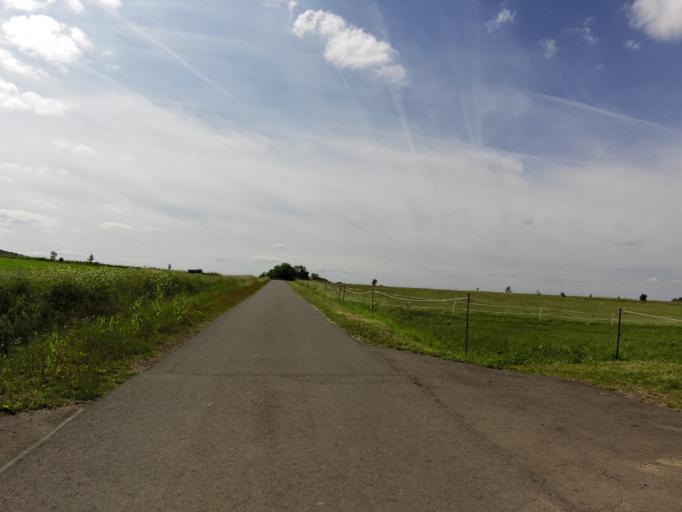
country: DE
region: Thuringia
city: Seebach
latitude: 50.9733
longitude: 10.4415
